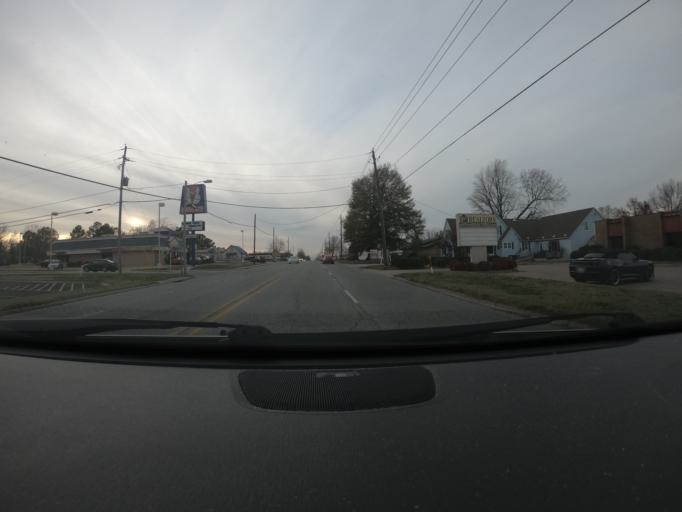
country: US
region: Arkansas
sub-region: Benton County
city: Rogers
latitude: 36.3337
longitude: -94.1292
